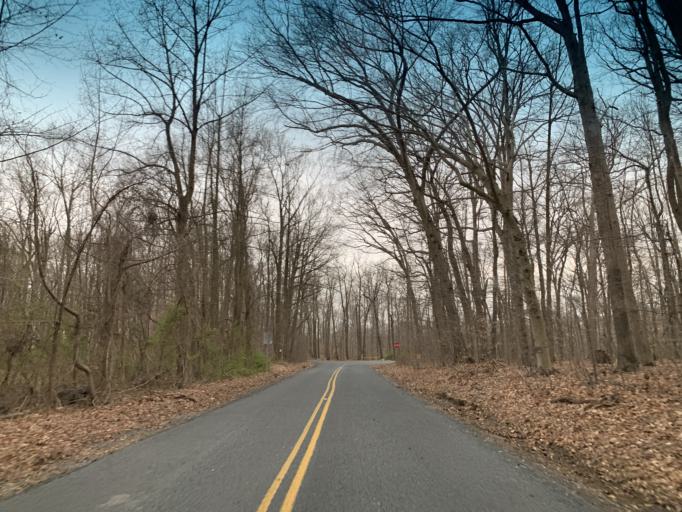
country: US
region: Maryland
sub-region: Harford County
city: Aberdeen
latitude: 39.5213
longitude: -76.2091
